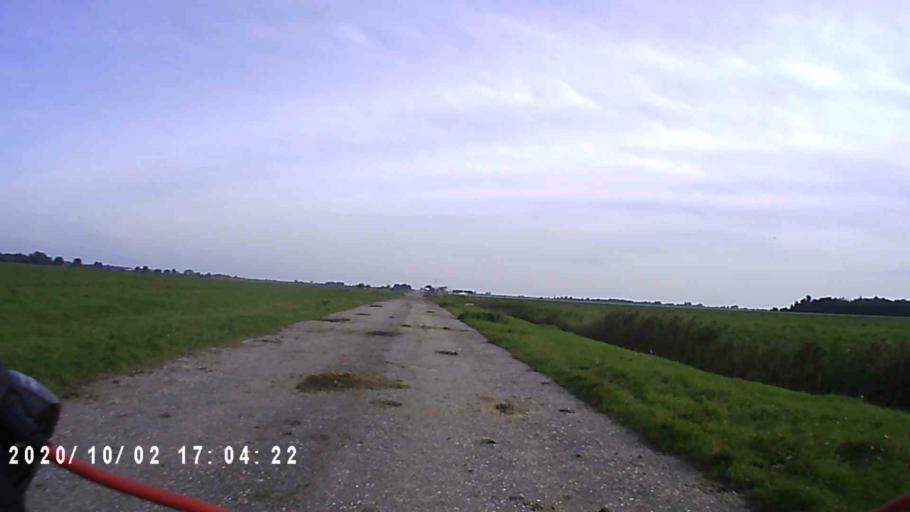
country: NL
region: Groningen
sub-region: Gemeente De Marne
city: Ulrum
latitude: 53.3400
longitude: 6.2674
